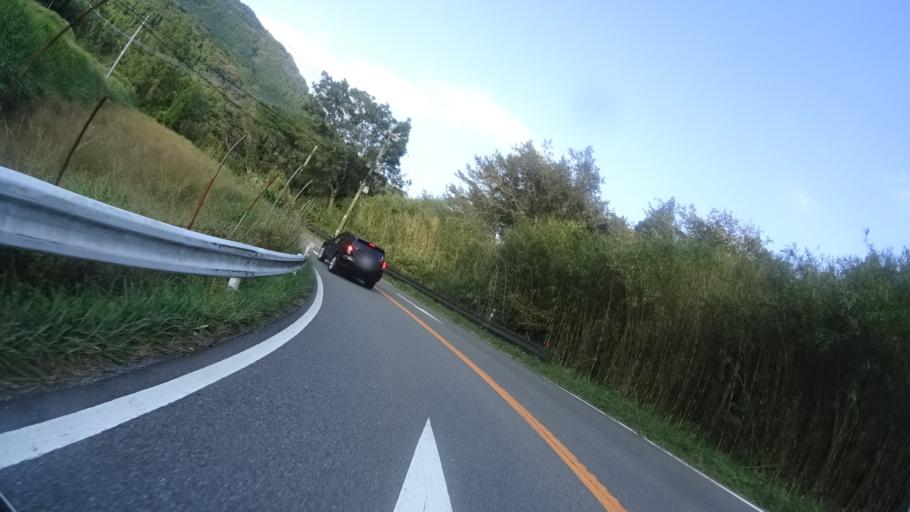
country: JP
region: Oita
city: Beppu
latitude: 33.2684
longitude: 131.4317
